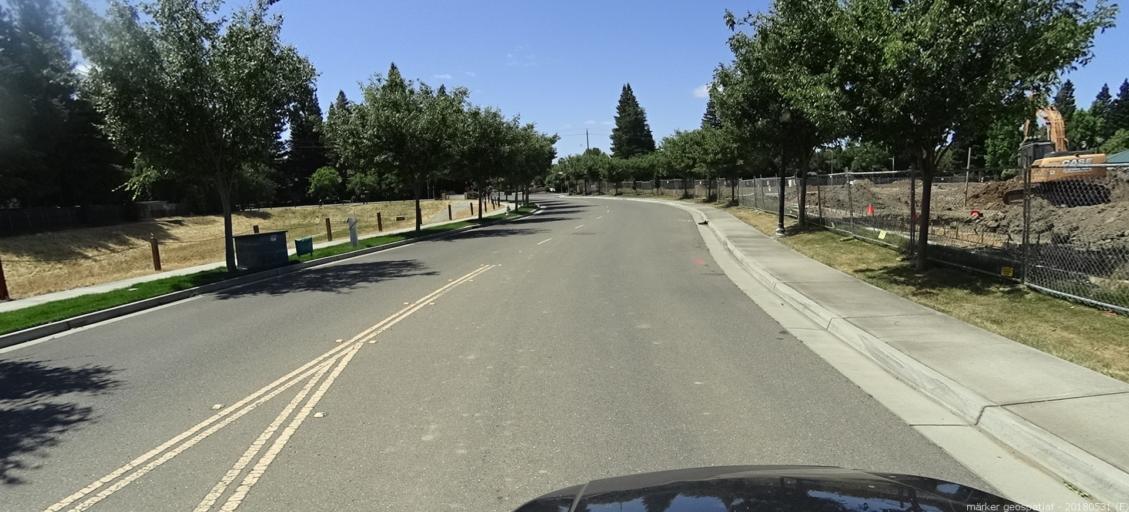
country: US
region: California
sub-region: Sacramento County
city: Sacramento
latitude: 38.6287
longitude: -121.5017
